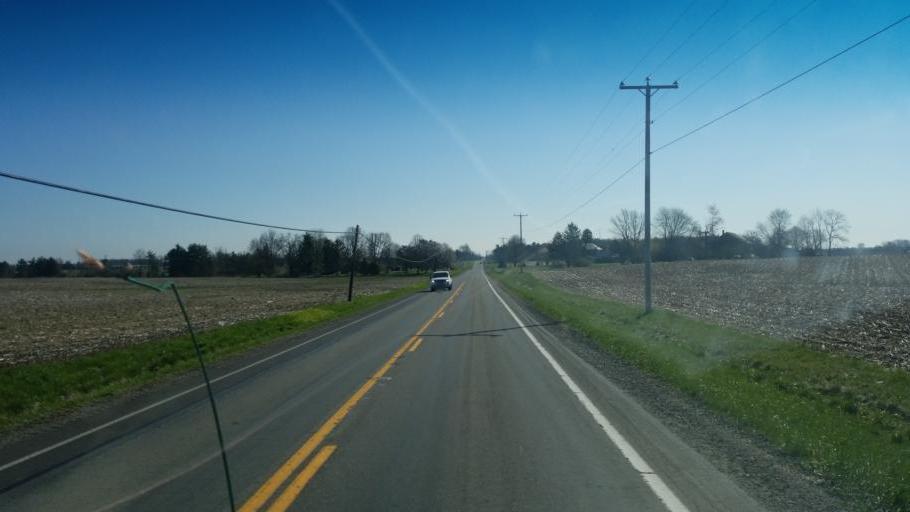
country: US
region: Ohio
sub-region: Hardin County
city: Kenton
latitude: 40.6600
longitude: -83.5693
